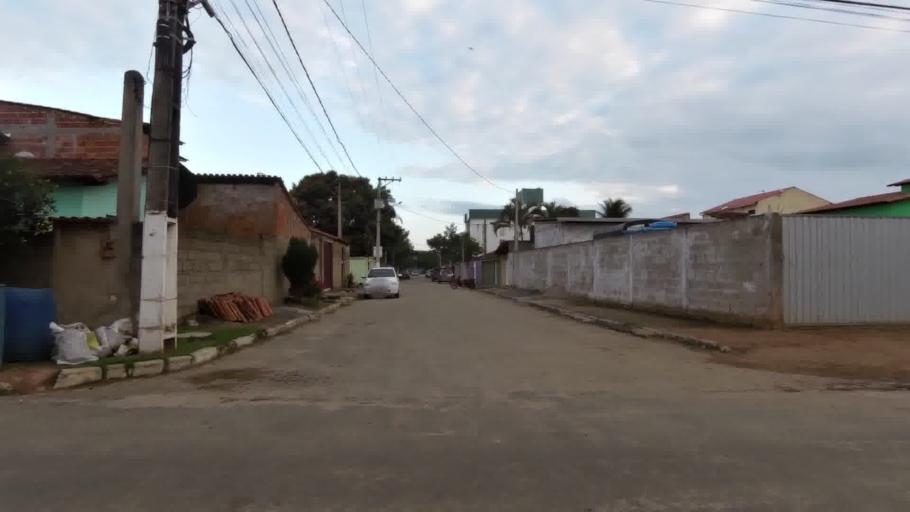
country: BR
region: Espirito Santo
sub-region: Piuma
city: Piuma
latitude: -20.8107
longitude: -40.6311
